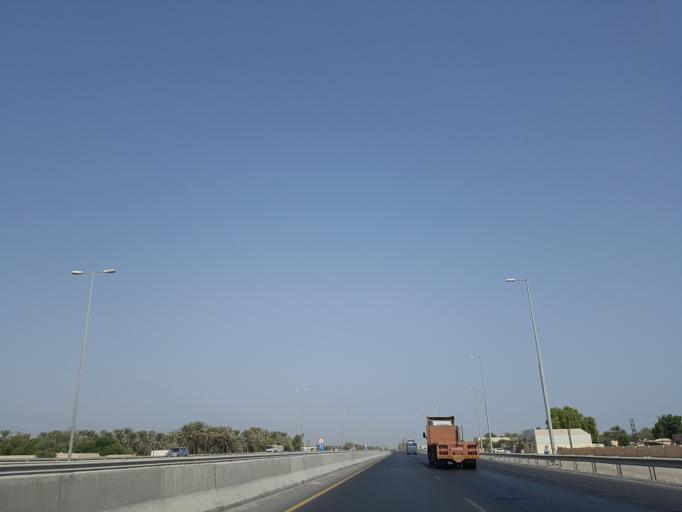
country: OM
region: Al Batinah
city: As Suwayq
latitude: 23.7628
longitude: 57.5529
